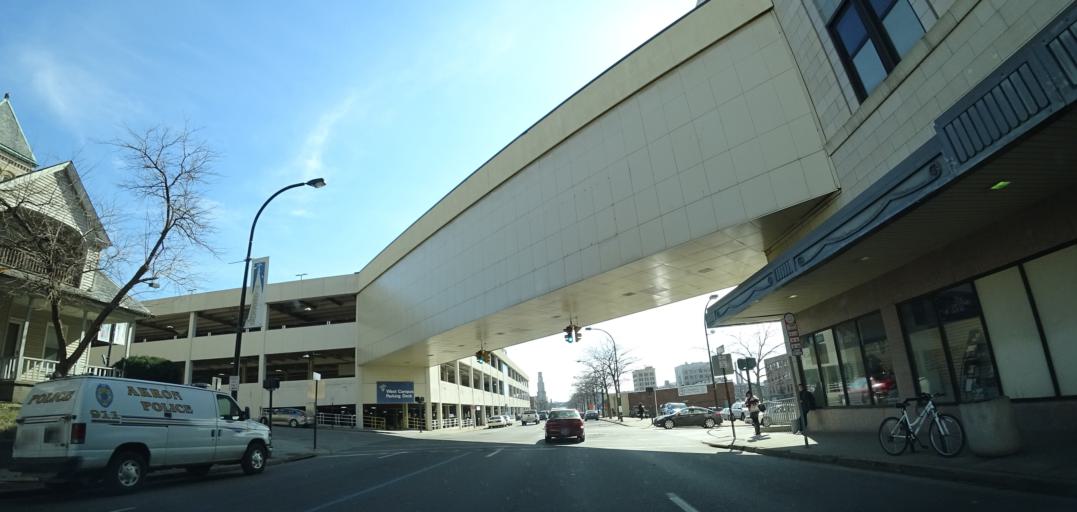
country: US
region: Ohio
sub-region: Summit County
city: Akron
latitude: 41.0787
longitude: -81.5191
